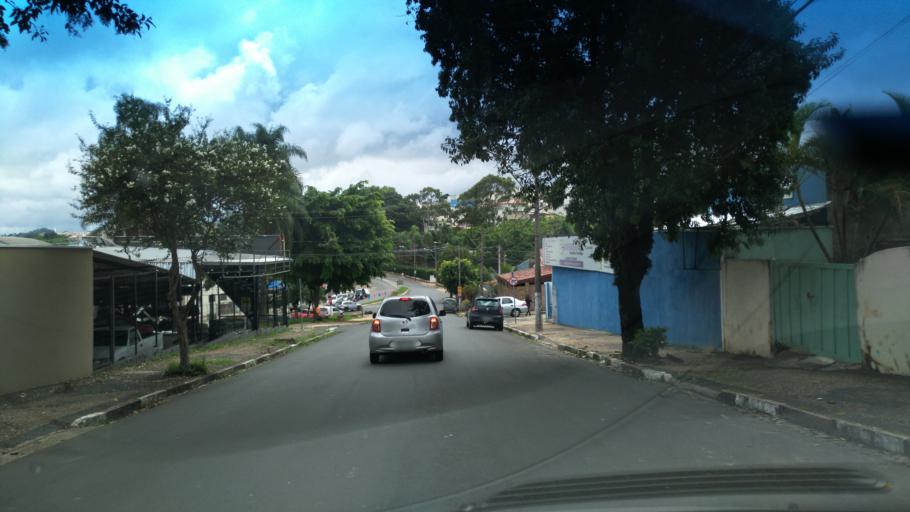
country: BR
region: Sao Paulo
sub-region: Valinhos
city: Valinhos
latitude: -22.9636
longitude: -46.9888
